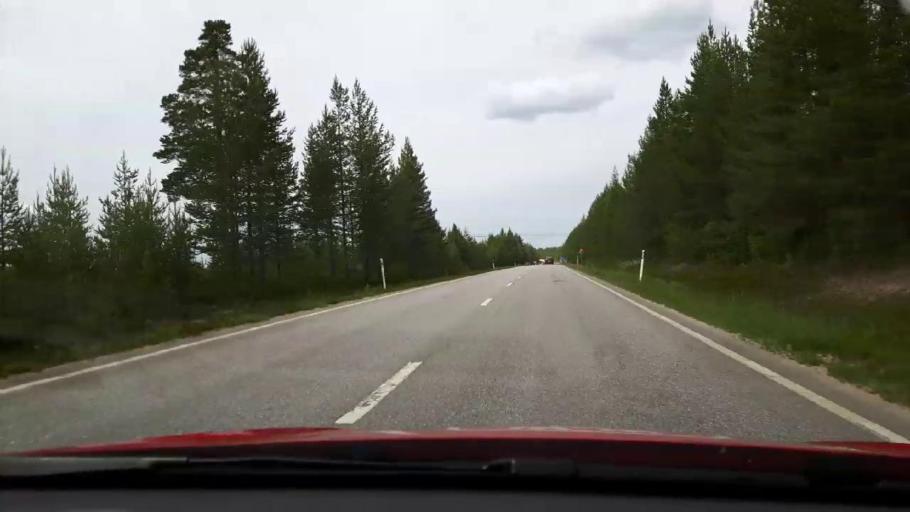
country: SE
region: Jaemtland
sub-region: Harjedalens Kommun
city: Sveg
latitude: 62.0528
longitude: 14.3084
